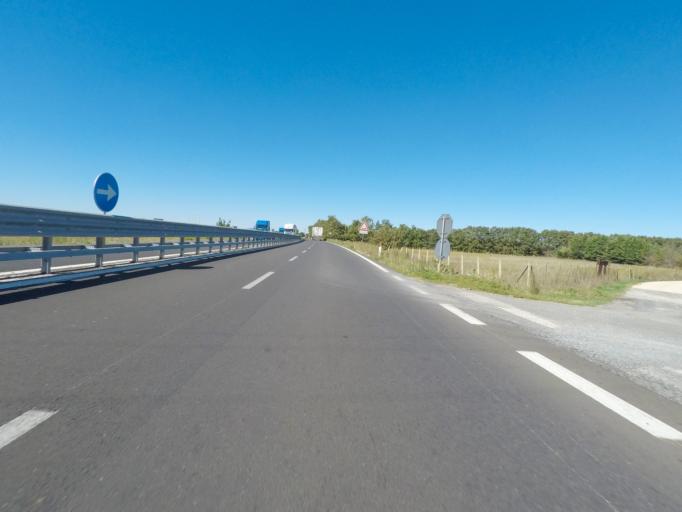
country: IT
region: Latium
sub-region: Provincia di Viterbo
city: Montalto di Castro
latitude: 42.3284
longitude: 11.6319
